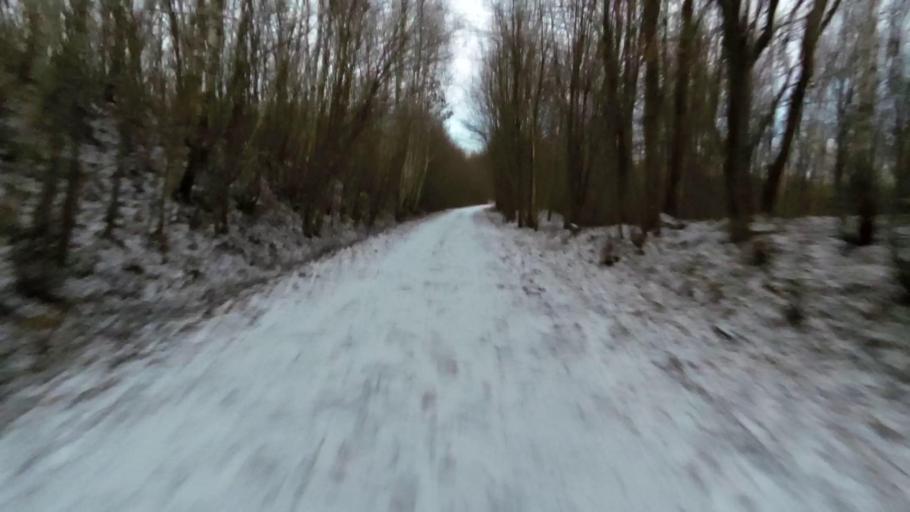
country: PL
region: West Pomeranian Voivodeship
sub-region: Powiat swidwinski
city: Polczyn-Zdroj
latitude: 53.7443
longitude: 16.0583
